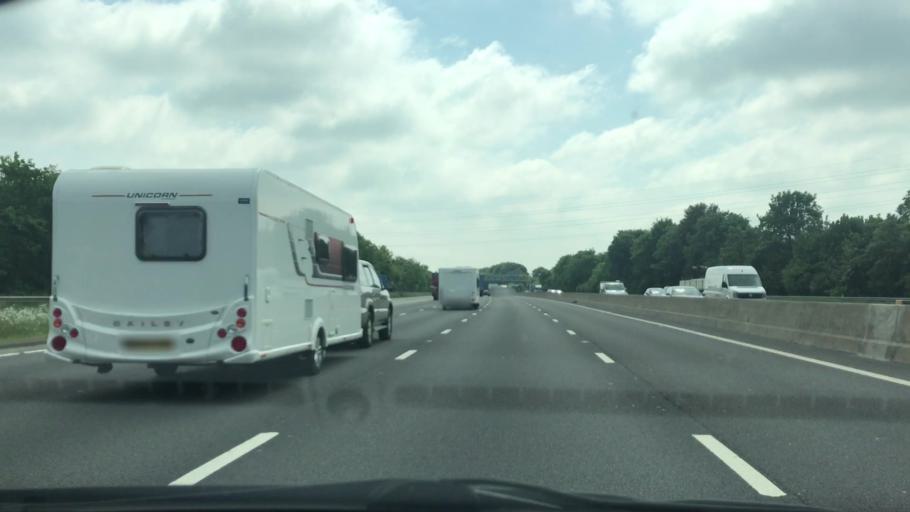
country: GB
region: England
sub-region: Derbyshire
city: Bolsover
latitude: 53.1953
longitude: -1.3235
